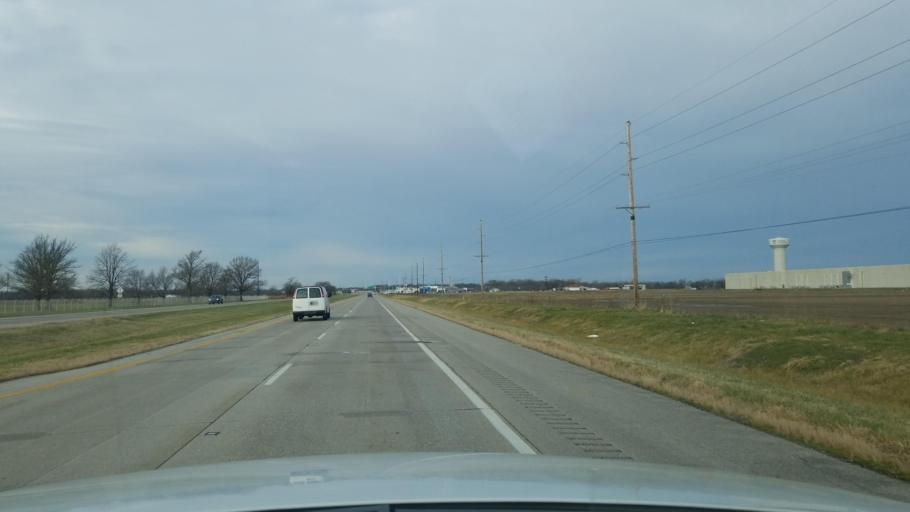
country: US
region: Indiana
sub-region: Posey County
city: Mount Vernon
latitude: 37.9429
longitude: -87.8409
